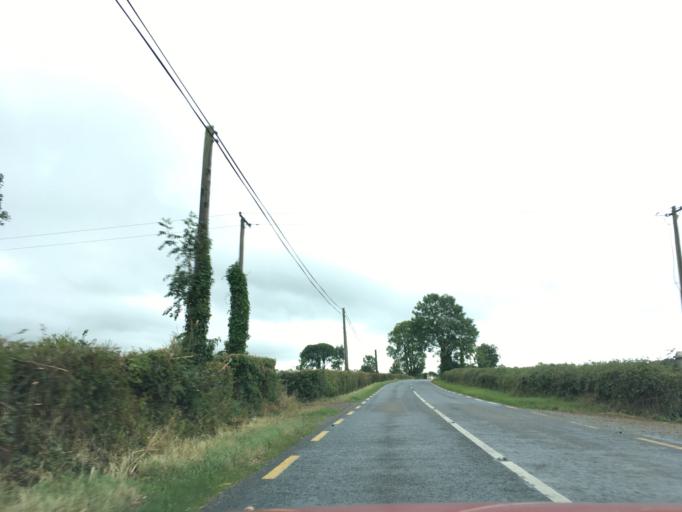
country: IE
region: Munster
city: Fethard
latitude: 52.4268
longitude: -7.7756
